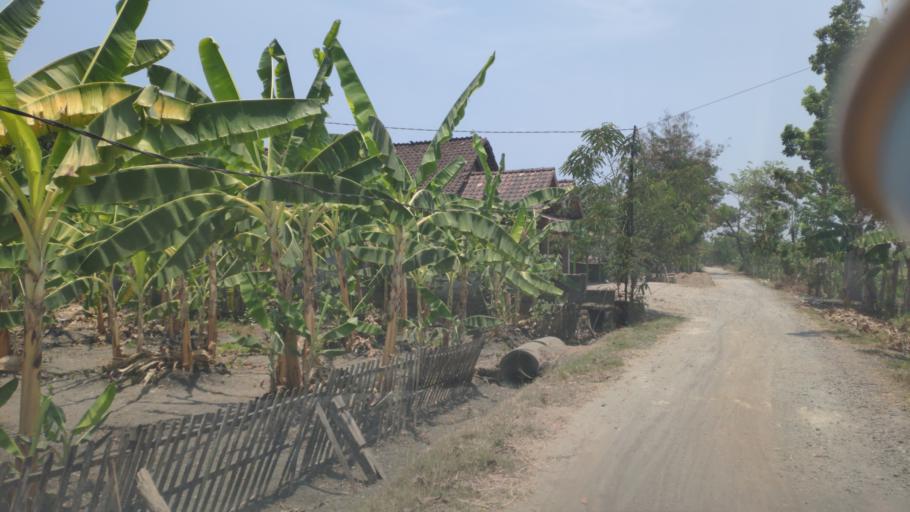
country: ID
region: Central Java
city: Temulus
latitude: -7.2265
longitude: 111.4300
